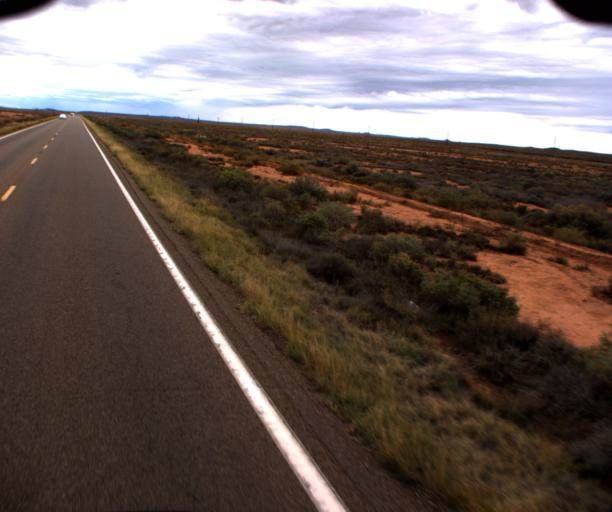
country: US
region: Arizona
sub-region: Navajo County
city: Holbrook
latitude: 34.8095
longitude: -110.1378
